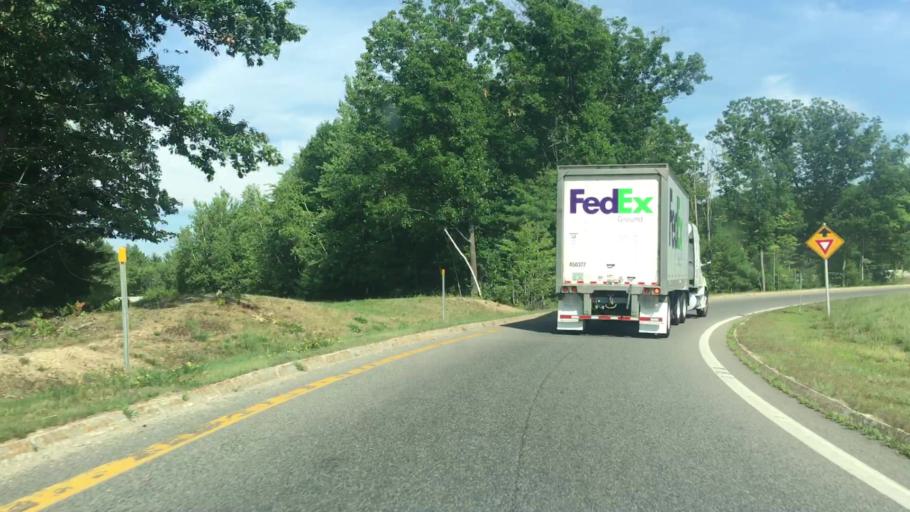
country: US
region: New Hampshire
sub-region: Strafford County
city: Rochester
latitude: 43.3292
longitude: -70.9865
